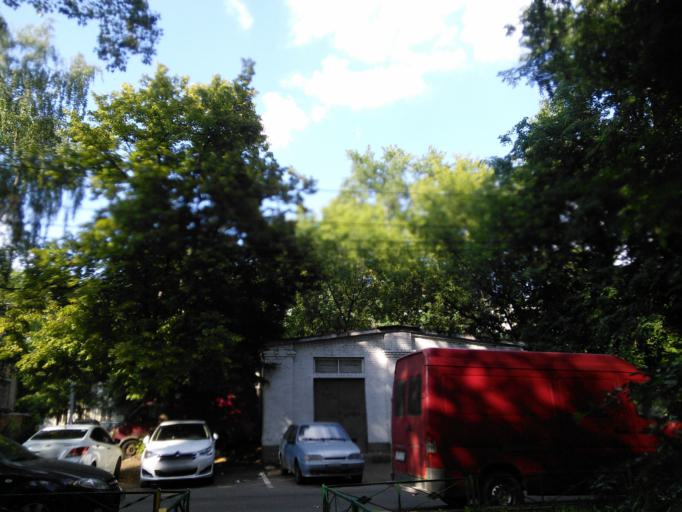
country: RU
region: Moskovskaya
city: Bogorodskoye
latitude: 55.8125
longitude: 37.7205
